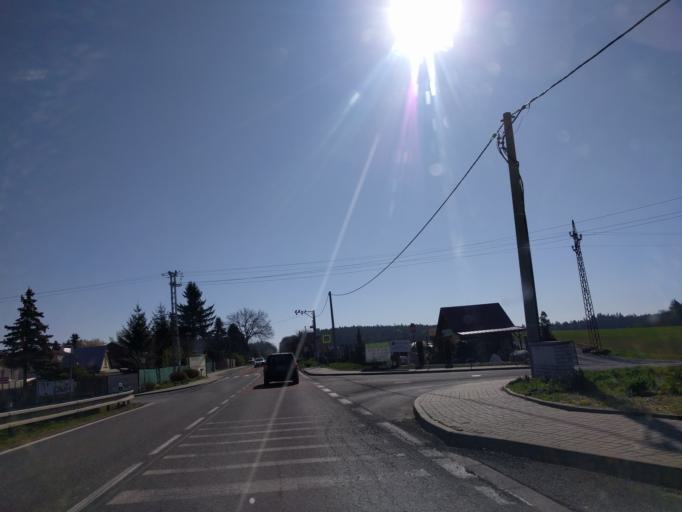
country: CZ
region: Central Bohemia
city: Mukarov
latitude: 49.9883
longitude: 14.7672
